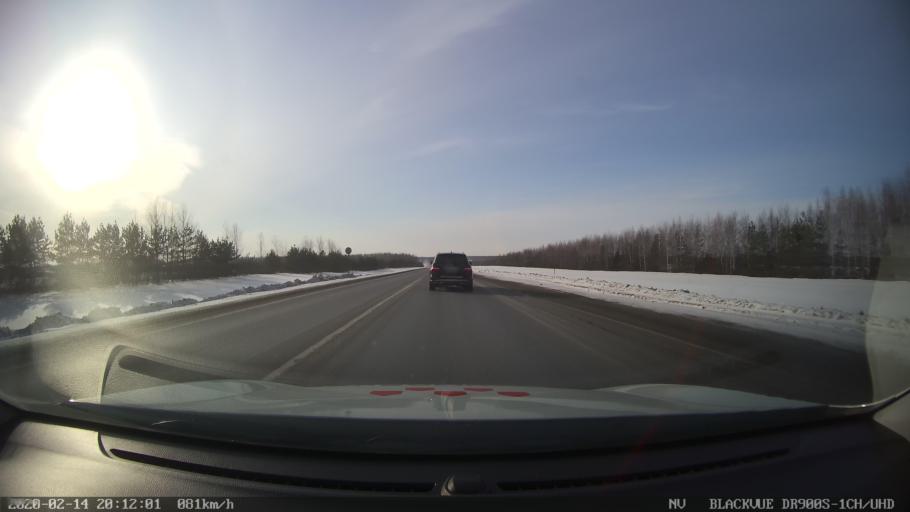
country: RU
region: Tatarstan
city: Verkhniy Uslon
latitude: 55.6706
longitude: 48.8669
